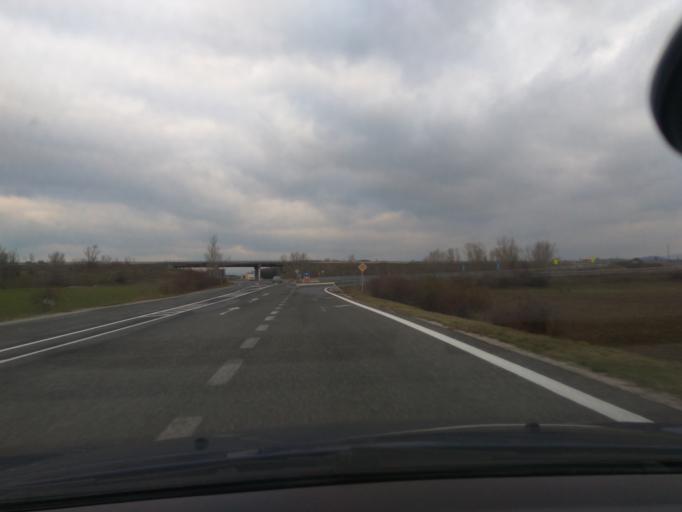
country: SK
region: Trnavsky
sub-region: Okres Trnava
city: Piestany
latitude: 48.6467
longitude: 17.8388
